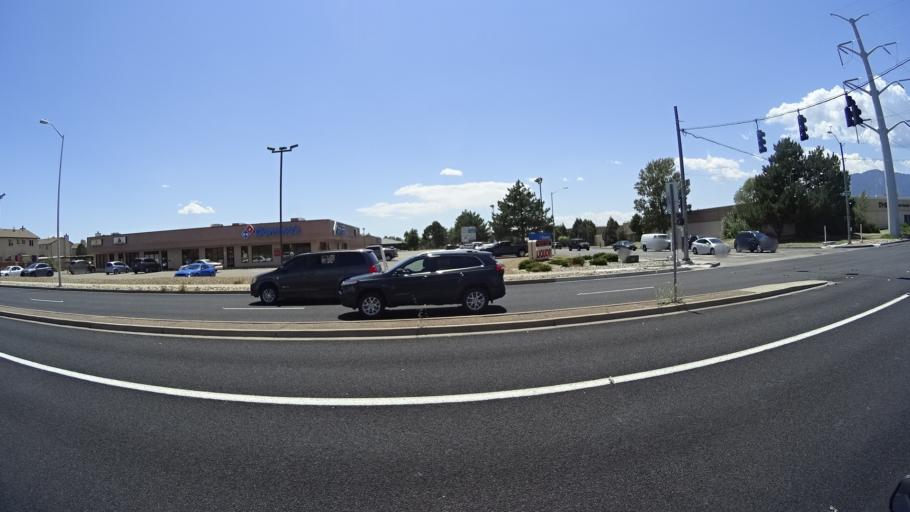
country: US
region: Colorado
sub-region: El Paso County
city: Stratmoor
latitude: 38.7891
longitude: -104.7538
